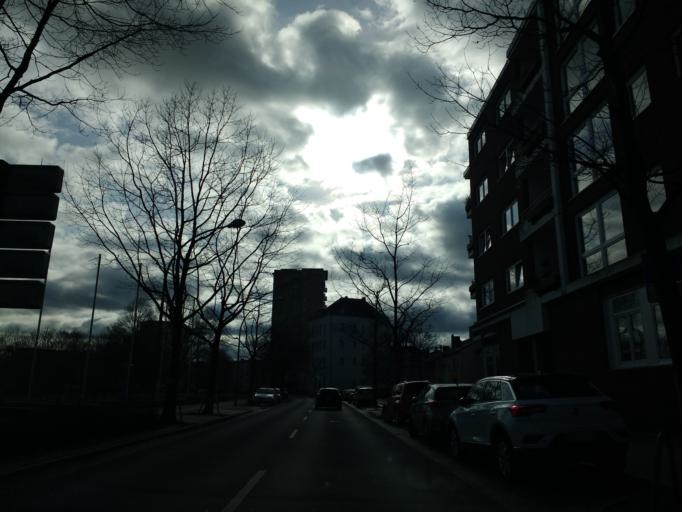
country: DE
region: Bremen
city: Bremerhaven
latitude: 53.5456
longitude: 8.5801
